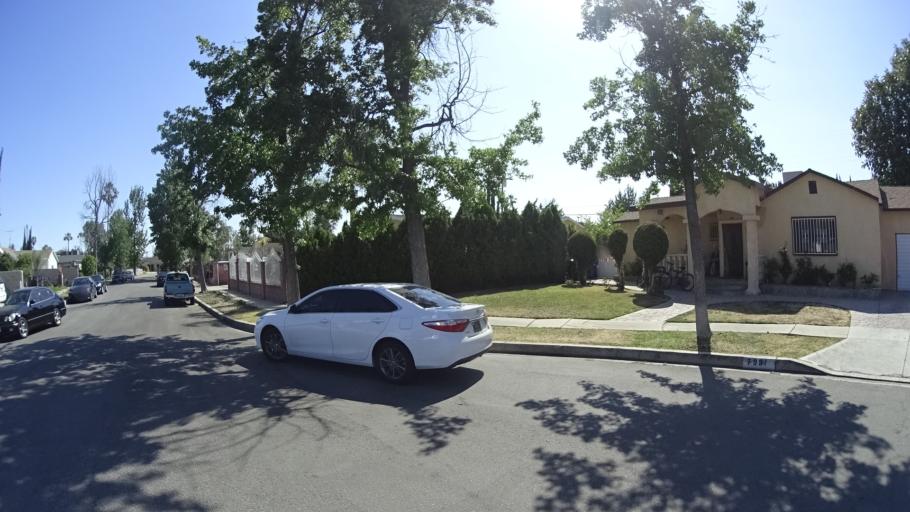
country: US
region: California
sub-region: Los Angeles County
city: Van Nuys
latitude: 34.2145
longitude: -118.4192
